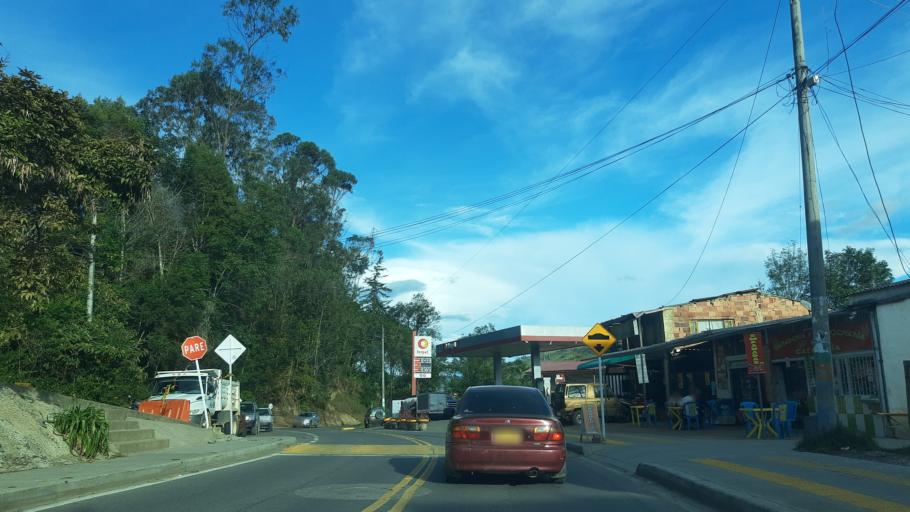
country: CO
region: Cundinamarca
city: Macheta
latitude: 5.0783
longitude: -73.6065
